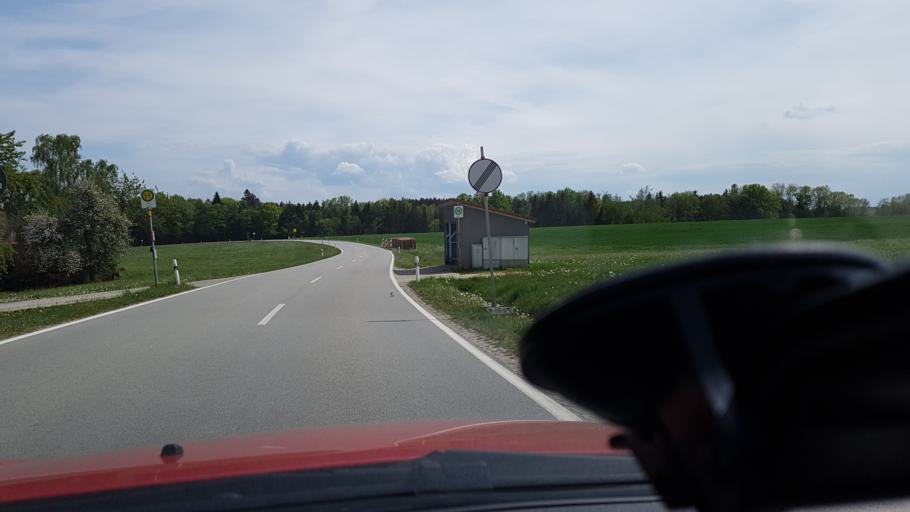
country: DE
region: Bavaria
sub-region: Lower Bavaria
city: Stubenberg
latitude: 48.3482
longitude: 13.0647
